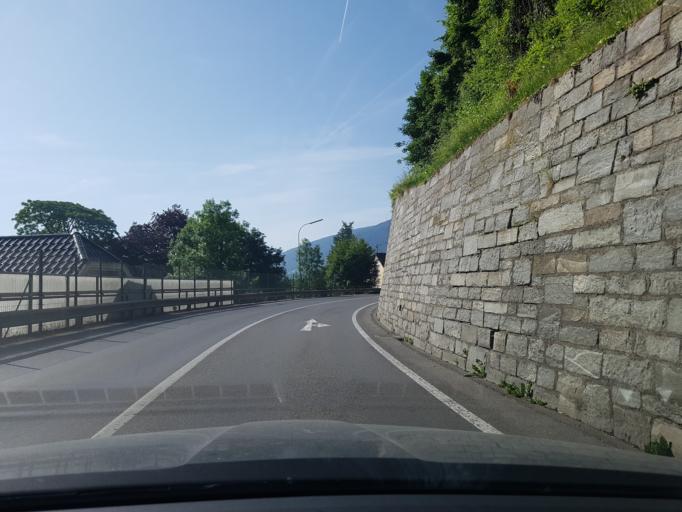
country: AT
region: Carinthia
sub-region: Politischer Bezirk Spittal an der Drau
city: Spittal an der Drau
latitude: 46.8015
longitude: 13.4978
